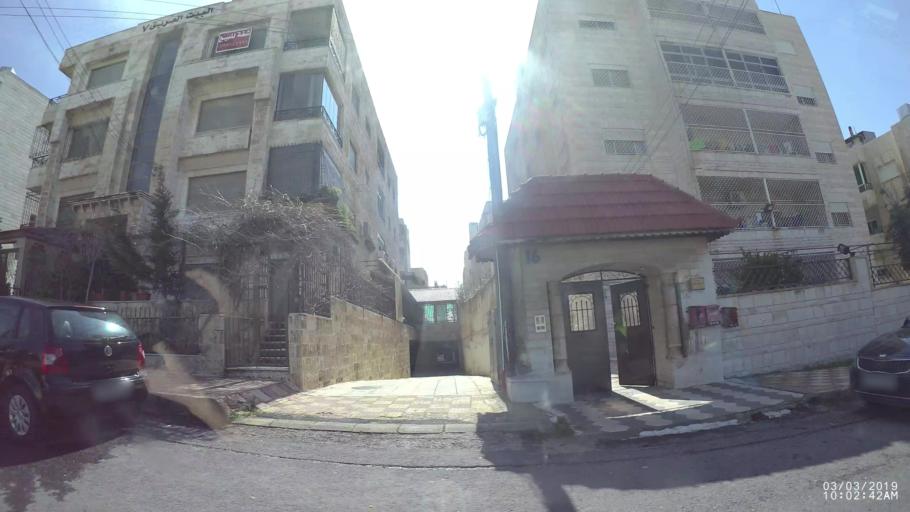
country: JO
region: Amman
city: Al Jubayhah
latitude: 31.9943
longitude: 35.8923
